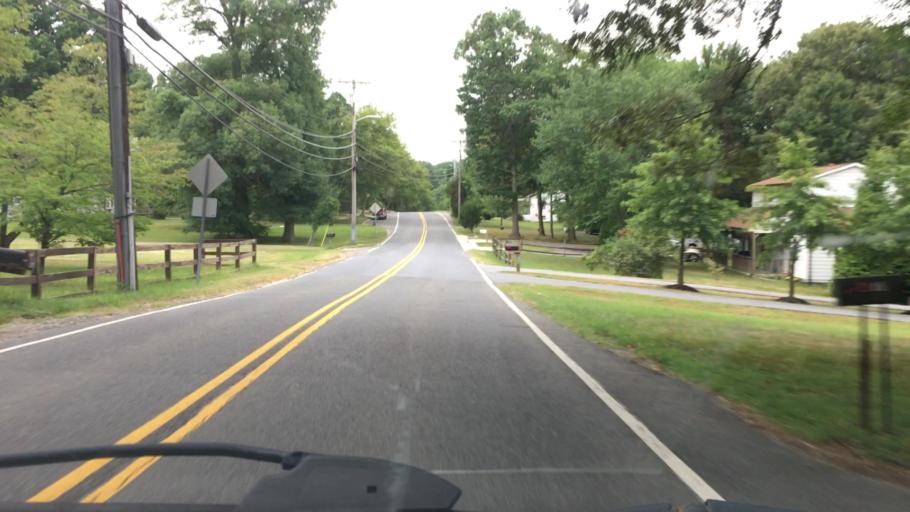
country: US
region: Maryland
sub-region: Prince George's County
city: Glenn Dale
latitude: 39.0017
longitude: -76.7783
